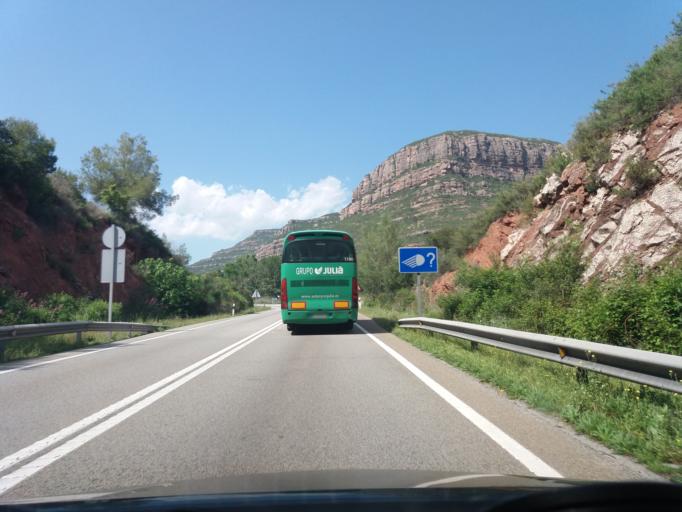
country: ES
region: Catalonia
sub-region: Provincia de Barcelona
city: Collbato
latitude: 41.5718
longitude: 1.8635
